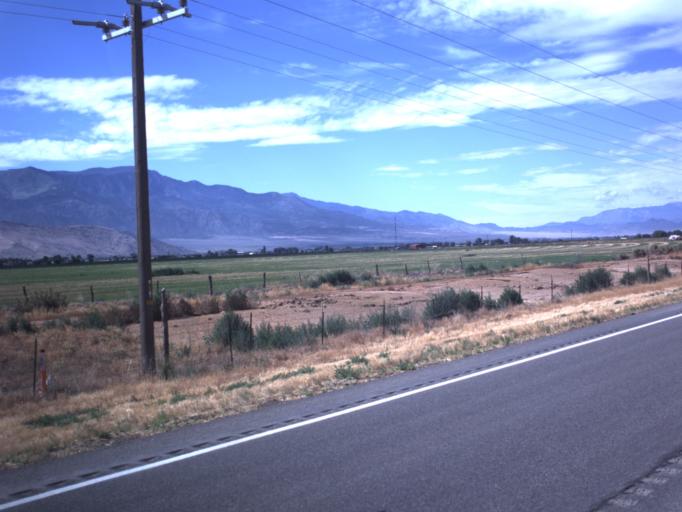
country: US
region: Utah
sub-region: Sevier County
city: Richfield
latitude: 38.7956
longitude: -112.0371
